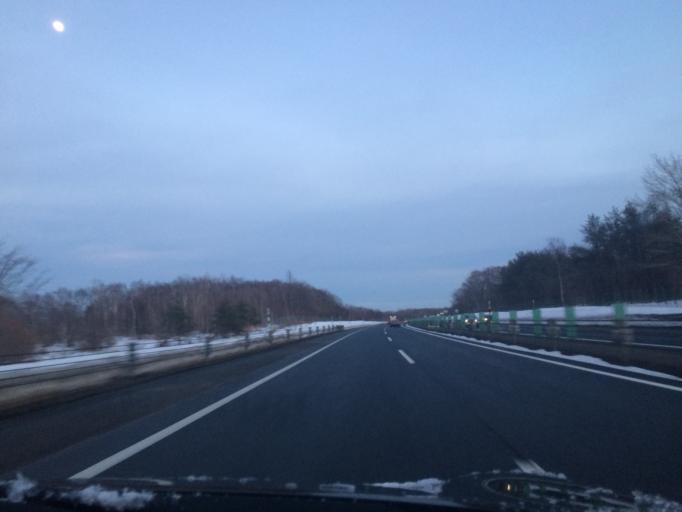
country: JP
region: Hokkaido
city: Chitose
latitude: 42.8395
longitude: 141.6012
